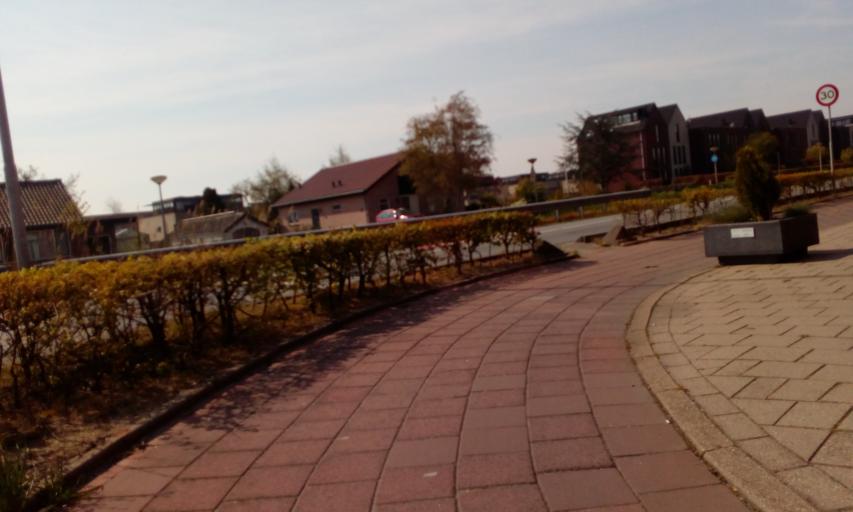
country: NL
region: South Holland
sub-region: Gemeente Delft
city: Delft
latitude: 52.0089
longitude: 4.3925
